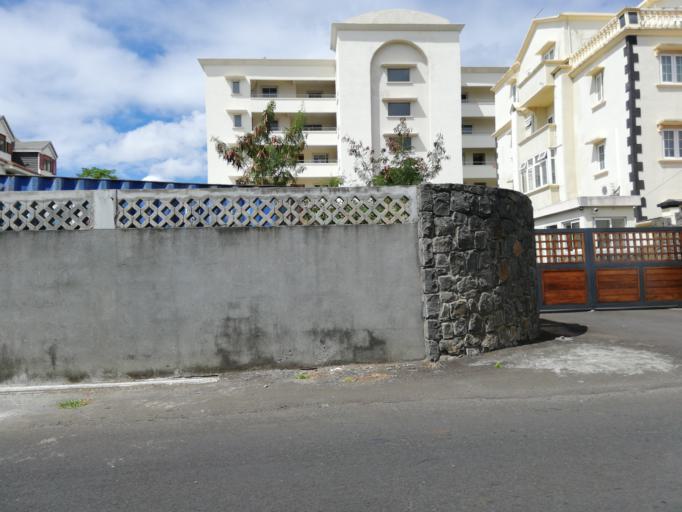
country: MU
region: Moka
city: Moka
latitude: -20.2175
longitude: 57.4756
